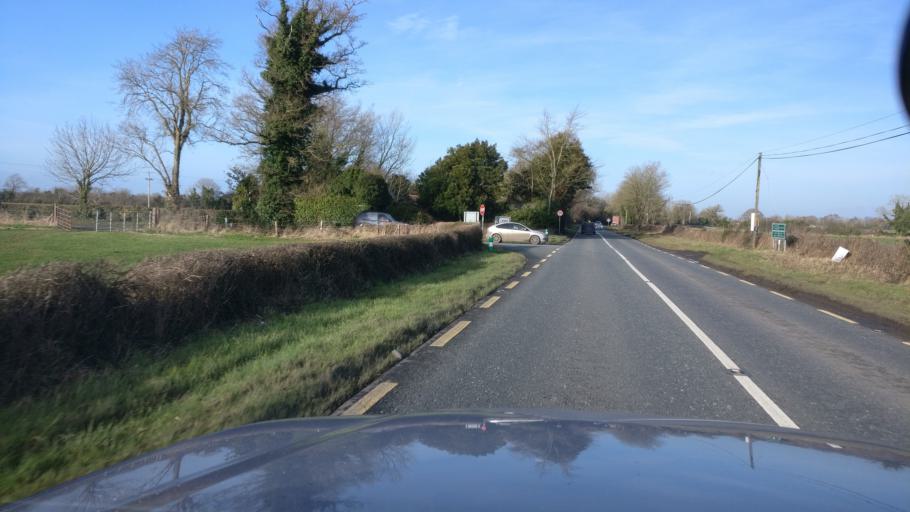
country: IE
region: Leinster
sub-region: Laois
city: Mountmellick
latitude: 53.1521
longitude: -7.3701
